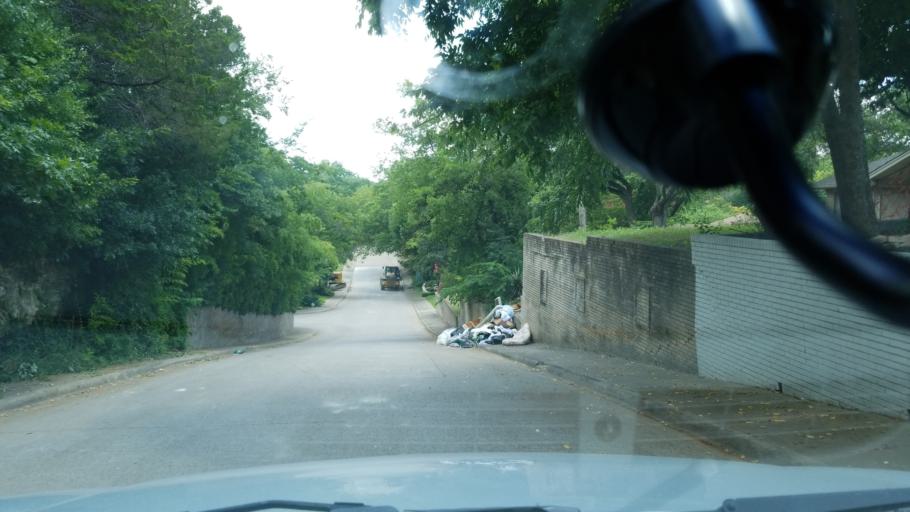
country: US
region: Texas
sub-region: Dallas County
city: Cockrell Hill
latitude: 32.7023
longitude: -96.8812
